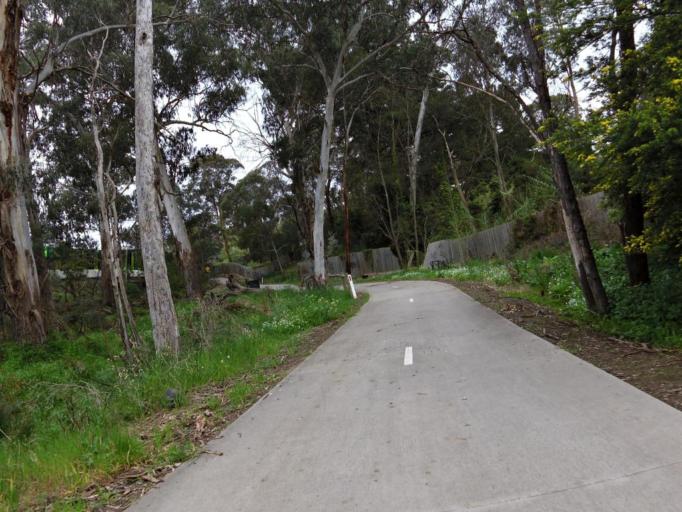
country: AU
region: Victoria
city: Mitcham
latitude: -37.8121
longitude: 145.2135
